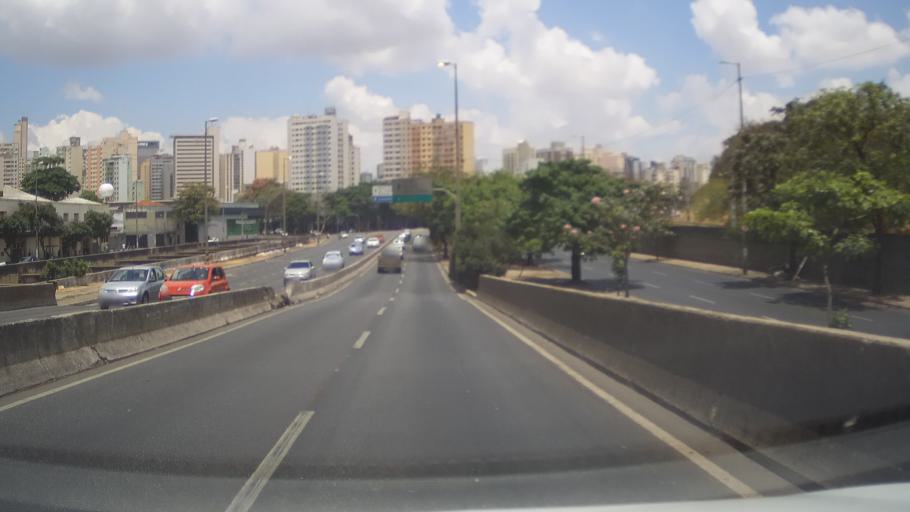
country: BR
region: Minas Gerais
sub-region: Belo Horizonte
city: Belo Horizonte
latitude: -19.9158
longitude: -43.9454
